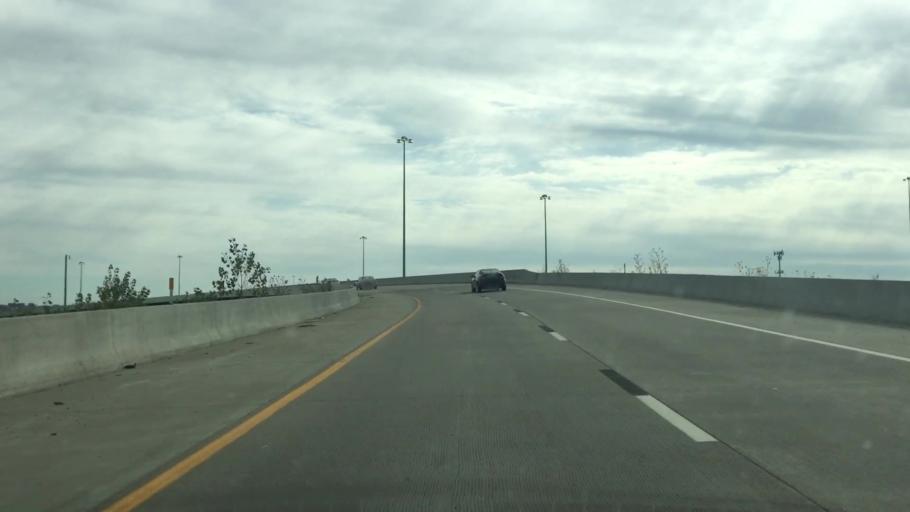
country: US
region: Kansas
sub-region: Johnson County
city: Lenexa
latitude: 38.9402
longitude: -94.7504
